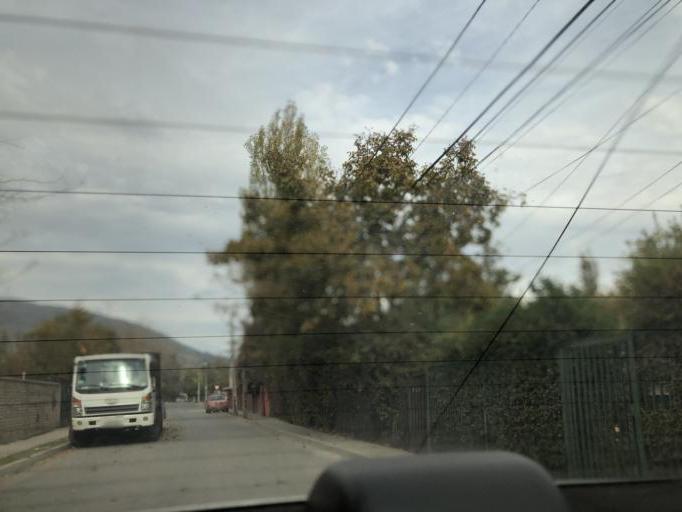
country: CL
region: Santiago Metropolitan
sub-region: Provincia de Cordillera
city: Puente Alto
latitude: -33.6077
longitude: -70.5285
